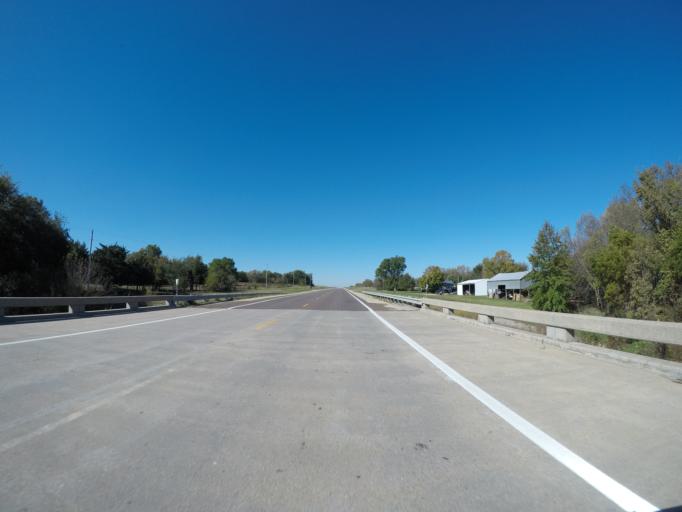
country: US
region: Kansas
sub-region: Riley County
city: Fort Riley North
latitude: 39.3061
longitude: -96.8550
